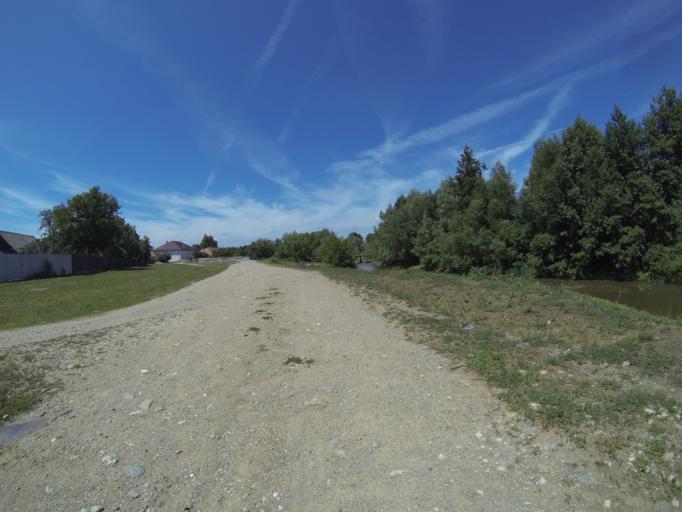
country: RO
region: Brasov
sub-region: Comuna Sinca Veche
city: Sinca Veche
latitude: 45.7613
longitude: 25.1706
